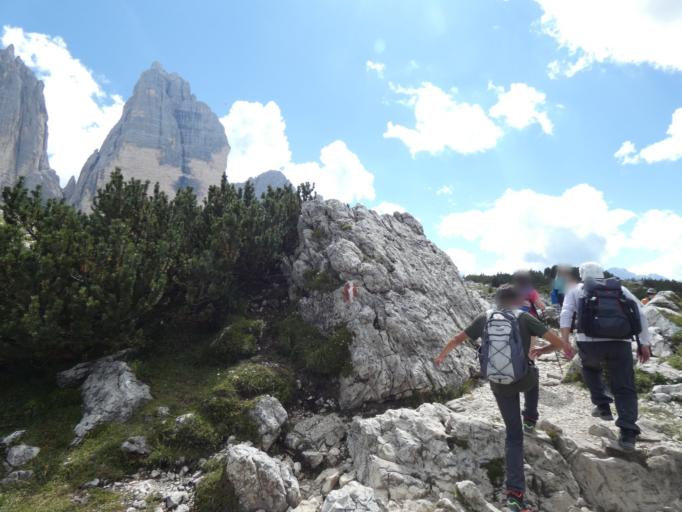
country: IT
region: Trentino-Alto Adige
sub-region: Bolzano
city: Sesto
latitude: 46.6291
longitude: 12.2957
